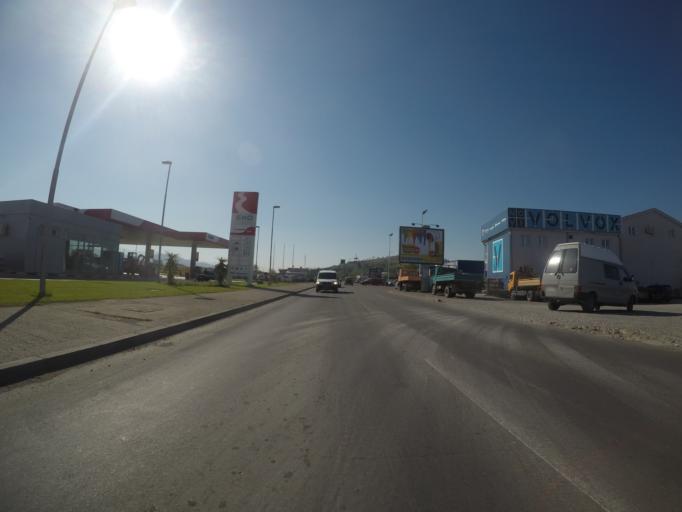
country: ME
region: Podgorica
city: Podgorica
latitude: 42.4302
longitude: 19.2315
